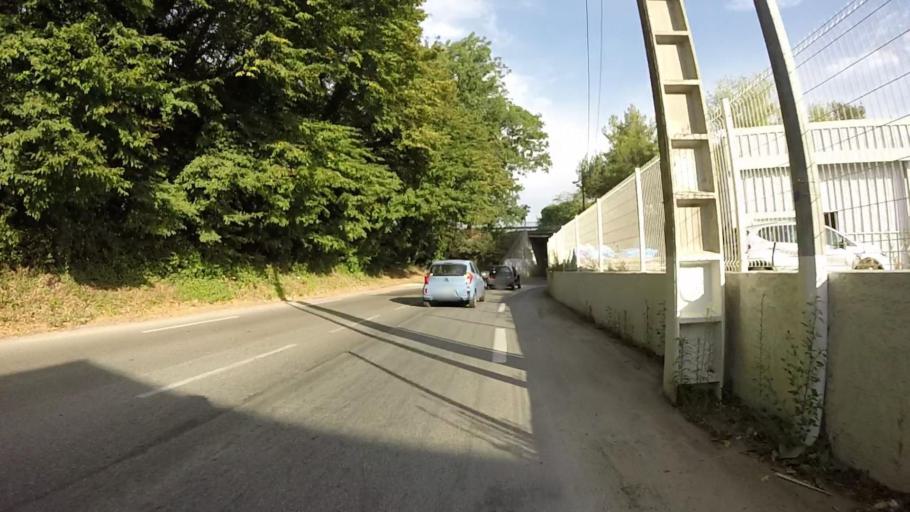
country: FR
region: Provence-Alpes-Cote d'Azur
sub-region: Departement des Alpes-Maritimes
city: Biot
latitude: 43.6113
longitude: 7.1093
